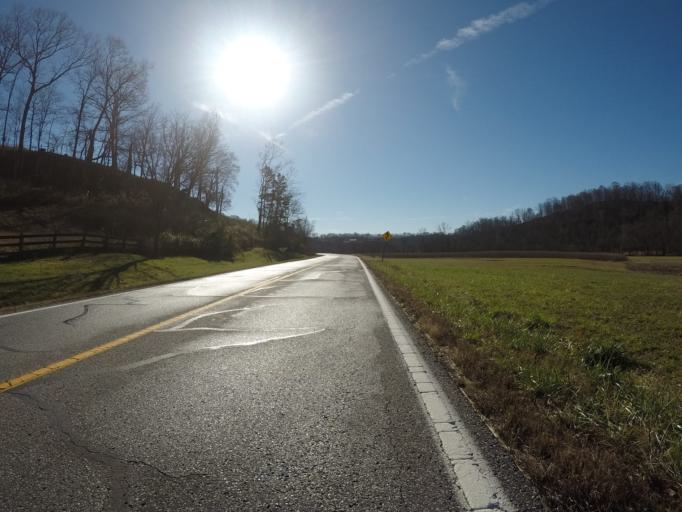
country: US
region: West Virginia
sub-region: Cabell County
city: Huntington
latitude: 38.4803
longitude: -82.4463
